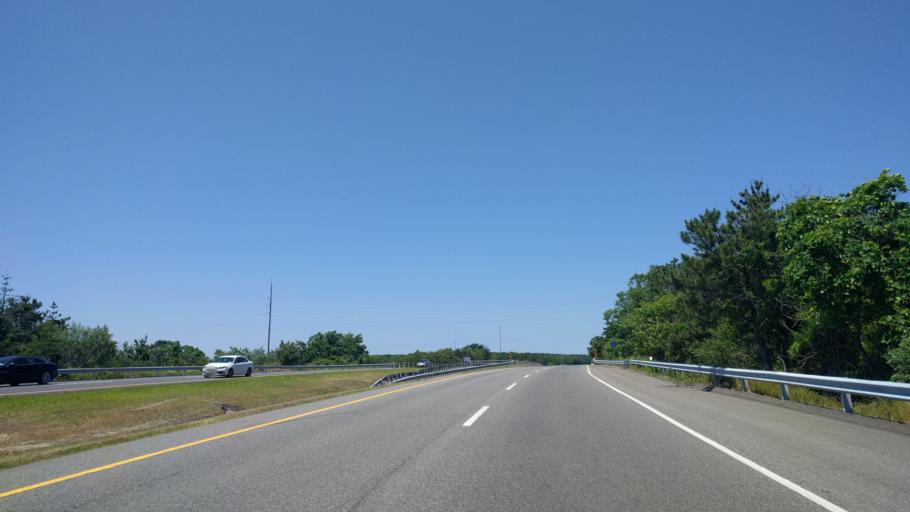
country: US
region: New York
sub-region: Suffolk County
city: Eastport
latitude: 40.8464
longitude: -72.7338
